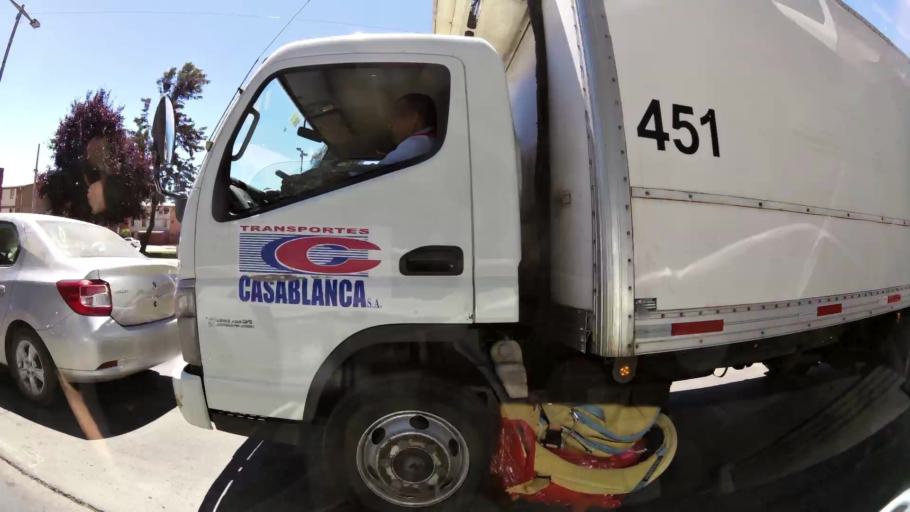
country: CL
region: O'Higgins
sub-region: Provincia de Cachapoal
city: Rancagua
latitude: -34.1587
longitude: -70.7197
